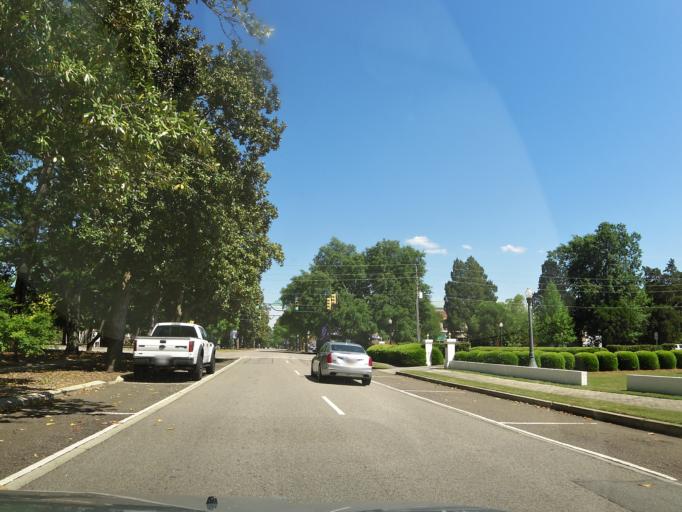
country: US
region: South Carolina
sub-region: Aiken County
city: Aiken
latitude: 33.5592
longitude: -81.7224
